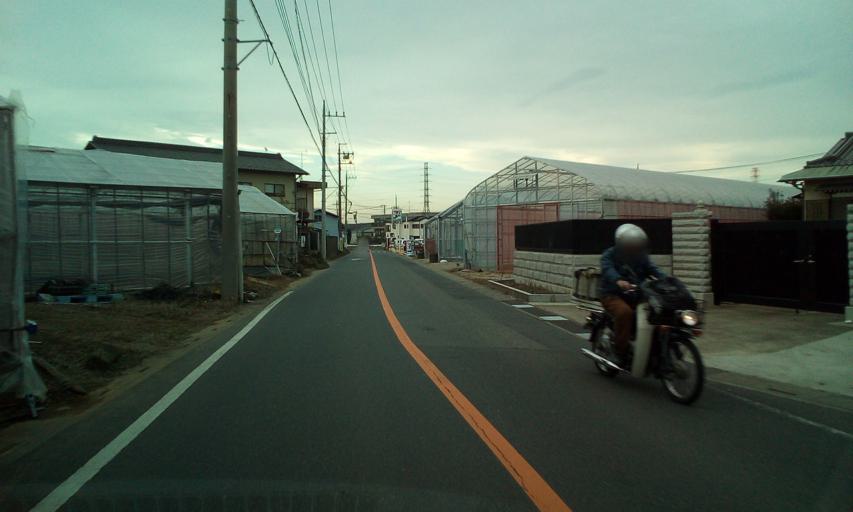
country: JP
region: Chiba
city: Nagareyama
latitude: 35.8426
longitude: 139.8802
